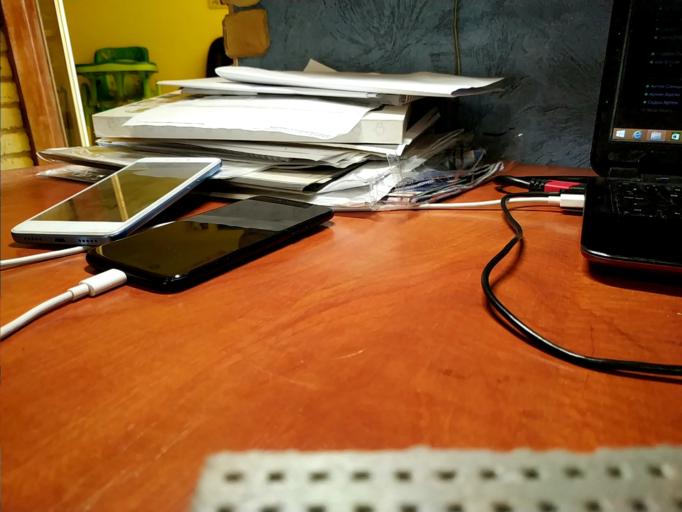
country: RU
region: Tverskaya
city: Spirovo
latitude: 57.4254
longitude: 35.0778
